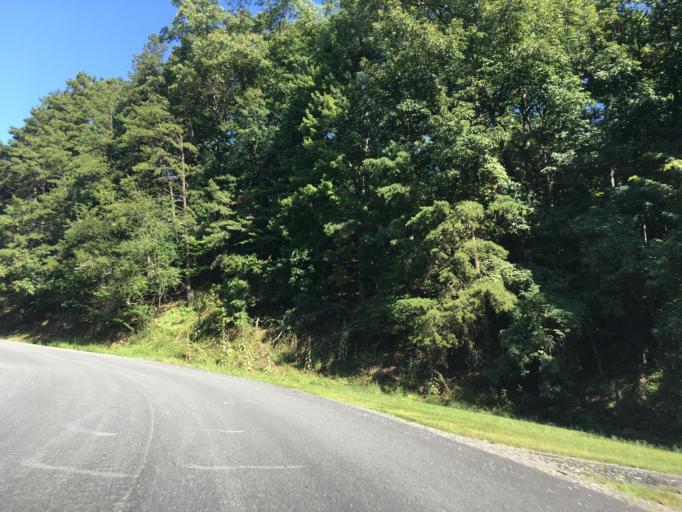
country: US
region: Pennsylvania
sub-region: York County
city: New Freedom
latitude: 39.6211
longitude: -76.7069
